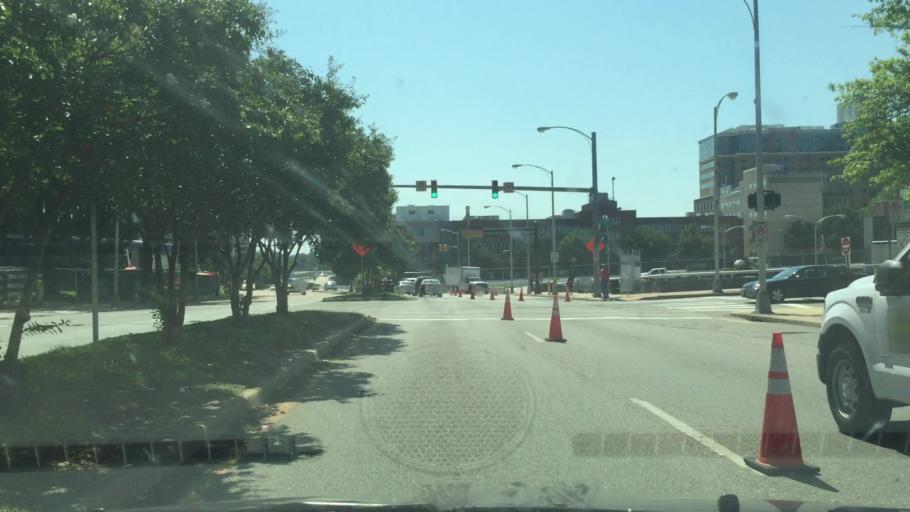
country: US
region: Virginia
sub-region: City of Richmond
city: Richmond
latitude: 37.5438
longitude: -77.4316
